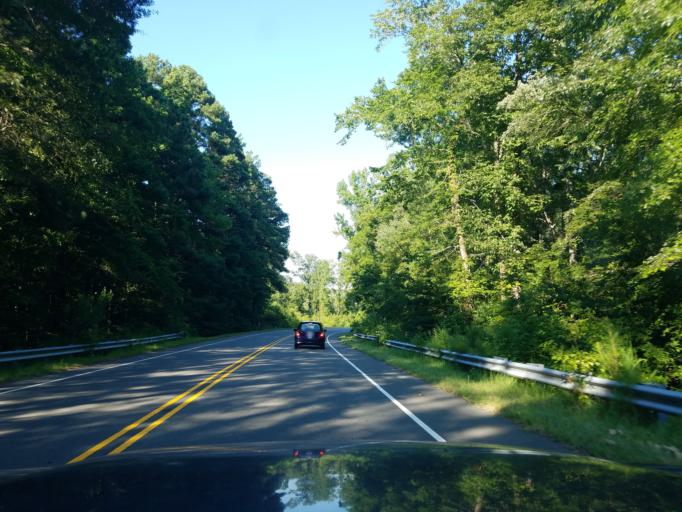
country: US
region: North Carolina
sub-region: Orange County
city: Chapel Hill
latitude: 35.8857
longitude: -78.9636
